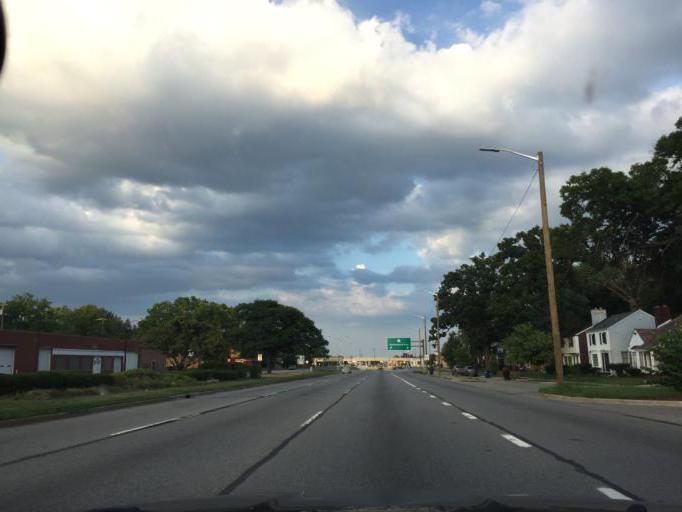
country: US
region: Michigan
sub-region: Oakland County
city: Ferndale
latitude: 42.4463
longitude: -83.1306
